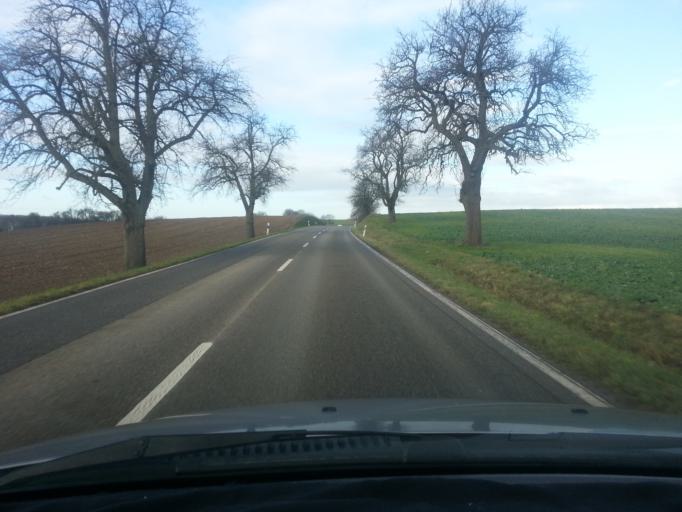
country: DE
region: Baden-Wuerttemberg
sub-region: Karlsruhe Region
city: Sulzfeld
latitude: 49.1655
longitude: 8.8582
